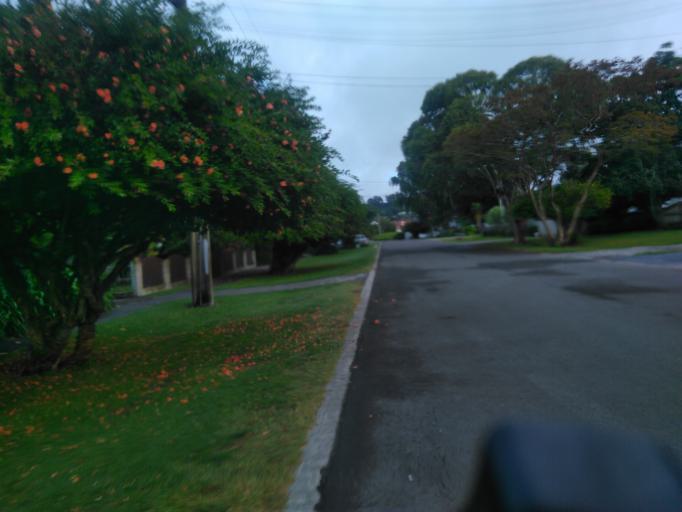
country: NZ
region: Gisborne
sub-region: Gisborne District
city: Gisborne
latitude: -38.6578
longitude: 178.0312
